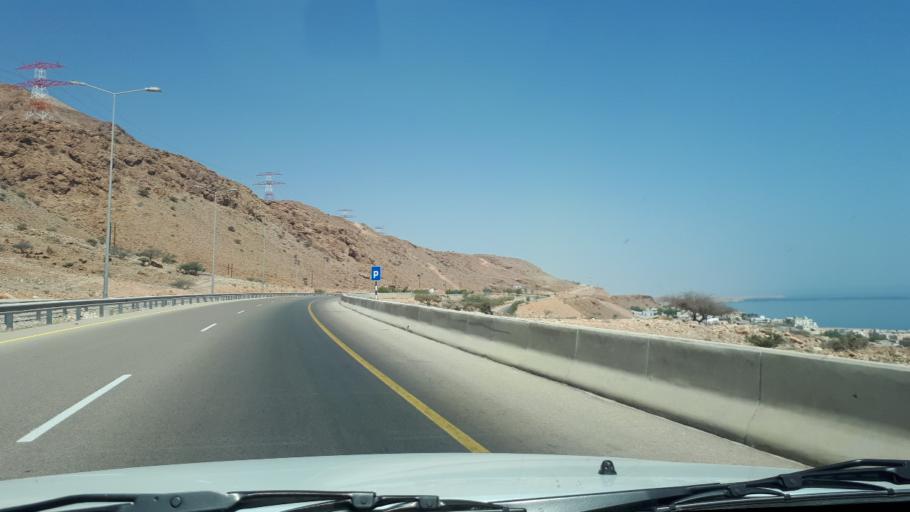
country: OM
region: Ash Sharqiyah
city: Sur
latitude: 22.8252
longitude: 59.2554
